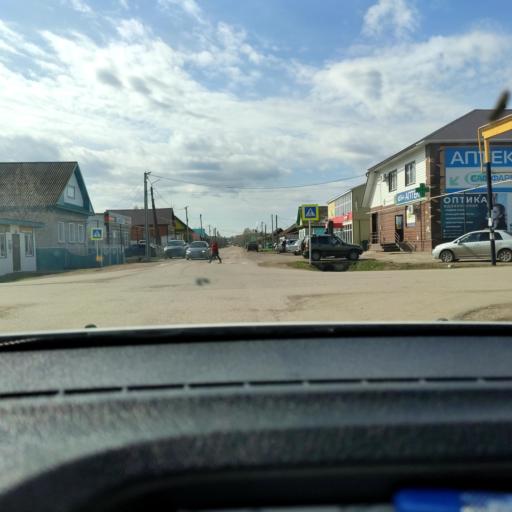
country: RU
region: Bashkortostan
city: Starobaltachevo
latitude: 56.0018
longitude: 55.9313
